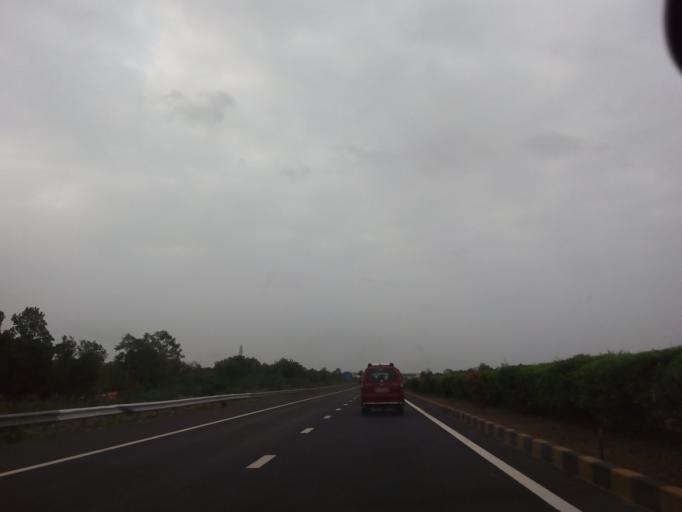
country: IN
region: Gujarat
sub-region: Kheda
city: Mahemdavad
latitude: 22.7957
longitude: 72.8406
